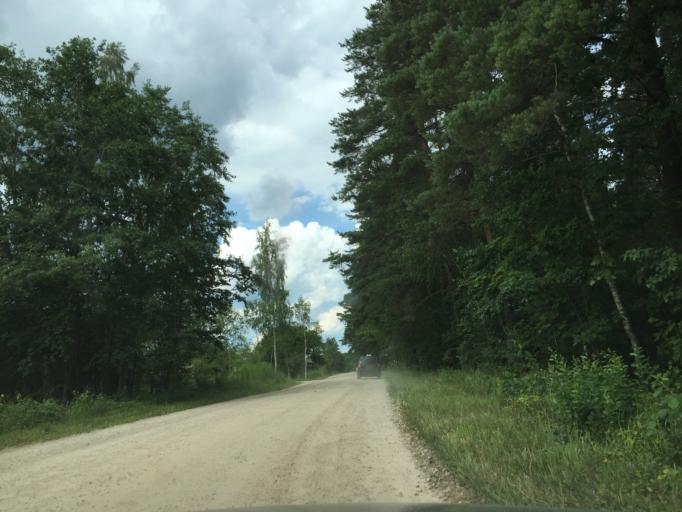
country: LV
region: Jelgava
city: Jelgava
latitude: 56.6287
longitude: 23.6227
